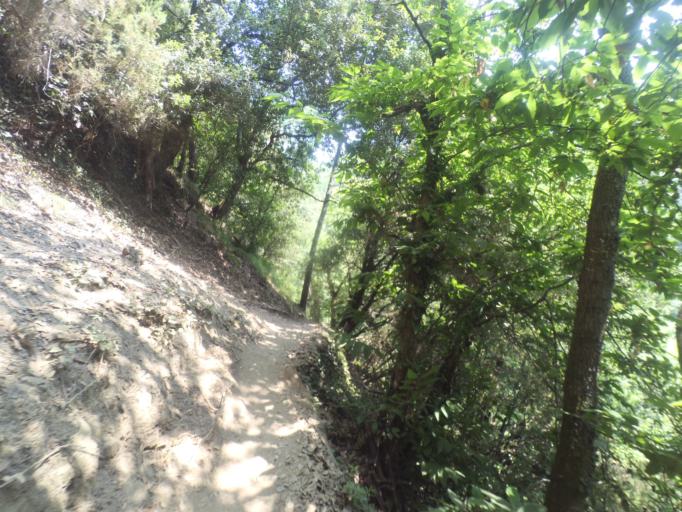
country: IT
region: Liguria
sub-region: Provincia di La Spezia
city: Riomaggiore
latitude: 44.1240
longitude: 9.7229
